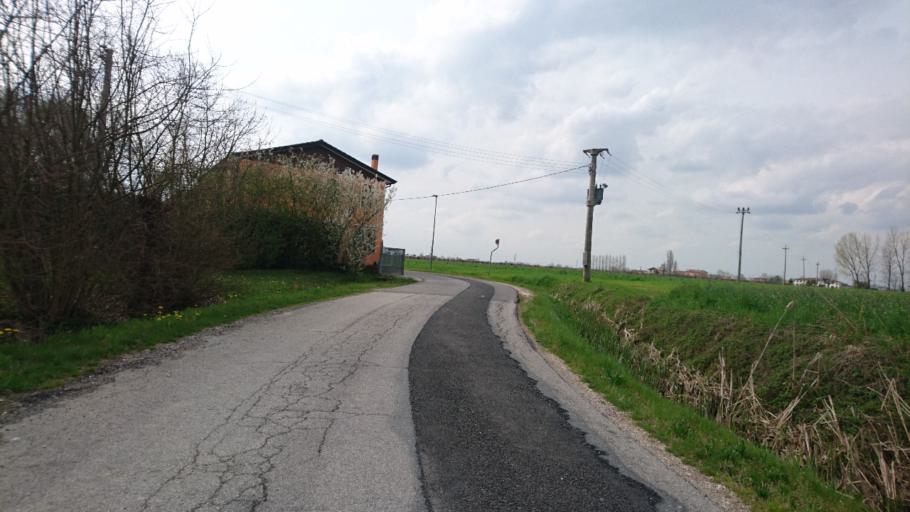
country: IT
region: Veneto
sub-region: Provincia di Padova
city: Tremignon
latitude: 45.4987
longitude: 11.8220
